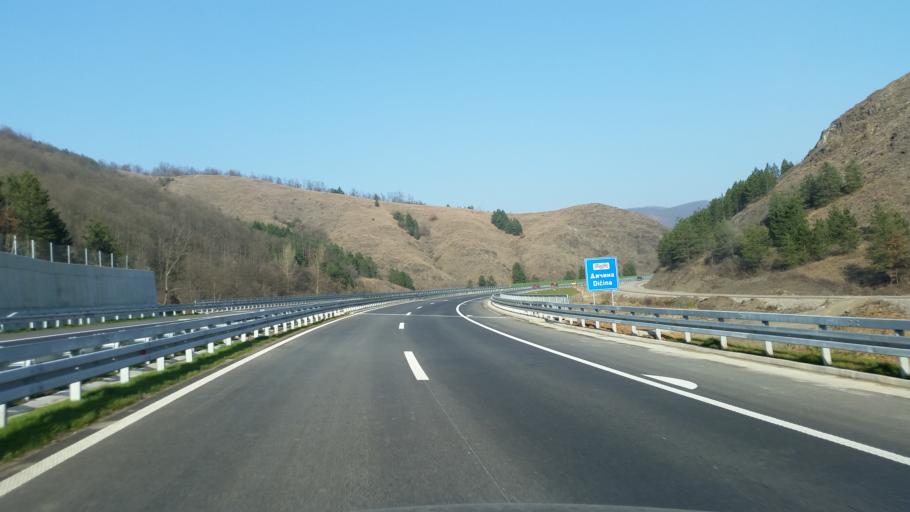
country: RS
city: Prislonica
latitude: 43.9901
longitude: 20.3995
